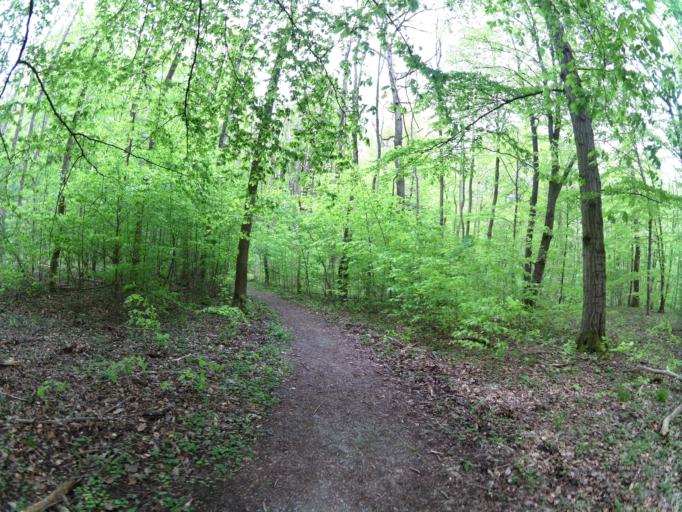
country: DE
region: Thuringia
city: Weberstedt
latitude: 51.0858
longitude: 10.5252
